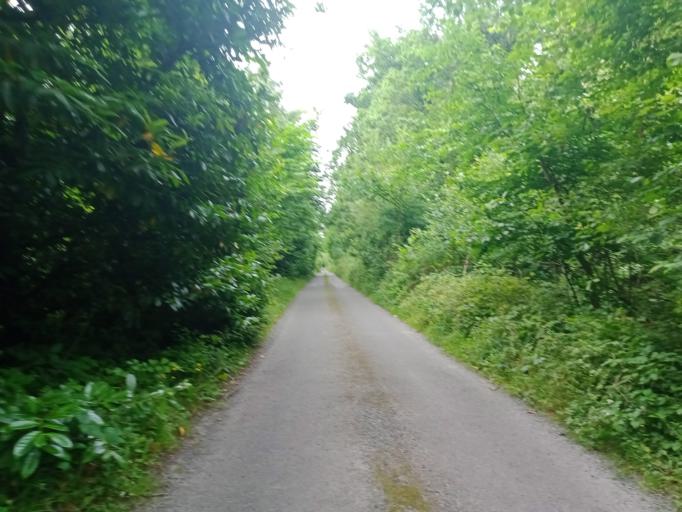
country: IE
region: Leinster
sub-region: Laois
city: Abbeyleix
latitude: 52.9044
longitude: -7.3614
